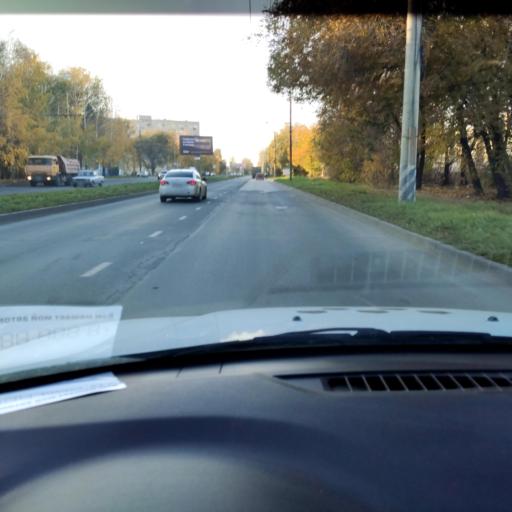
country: RU
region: Samara
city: Tol'yatti
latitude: 53.5140
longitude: 49.4466
